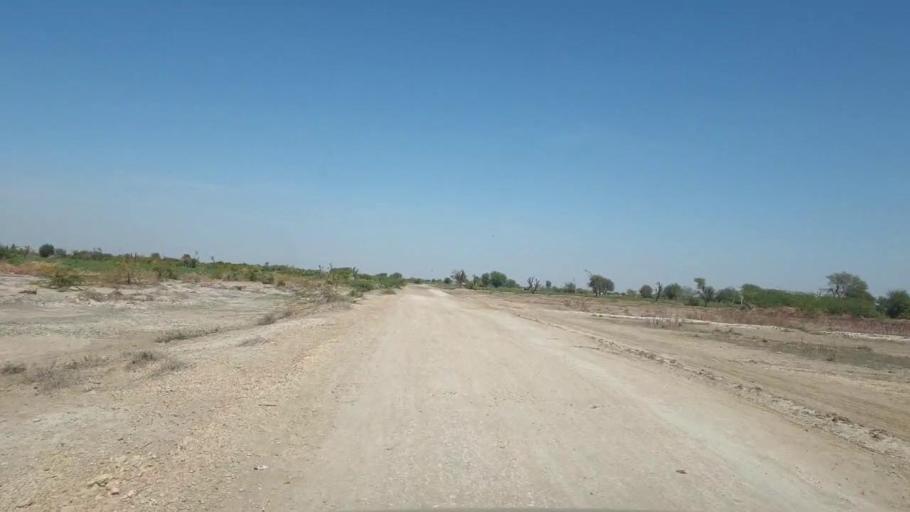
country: PK
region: Sindh
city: Dhoro Naro
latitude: 25.4110
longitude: 69.6168
